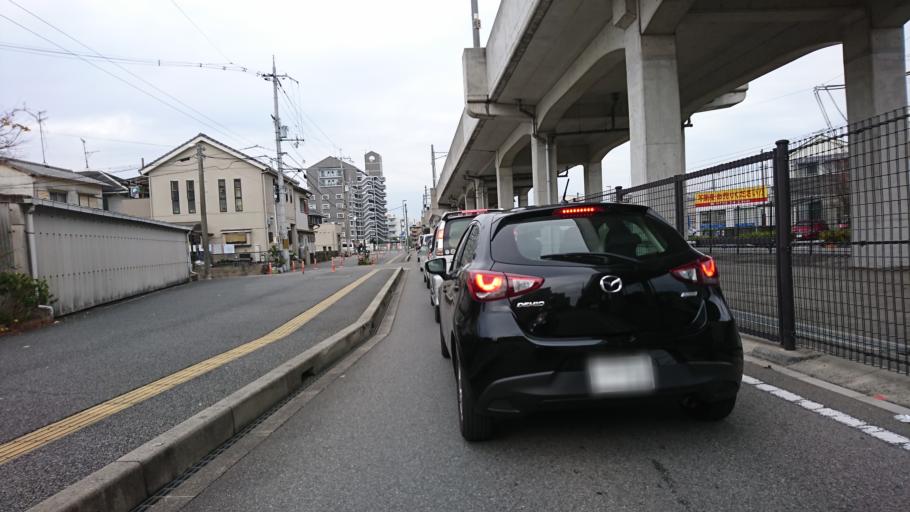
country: JP
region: Hyogo
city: Kakogawacho-honmachi
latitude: 34.7627
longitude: 134.8456
